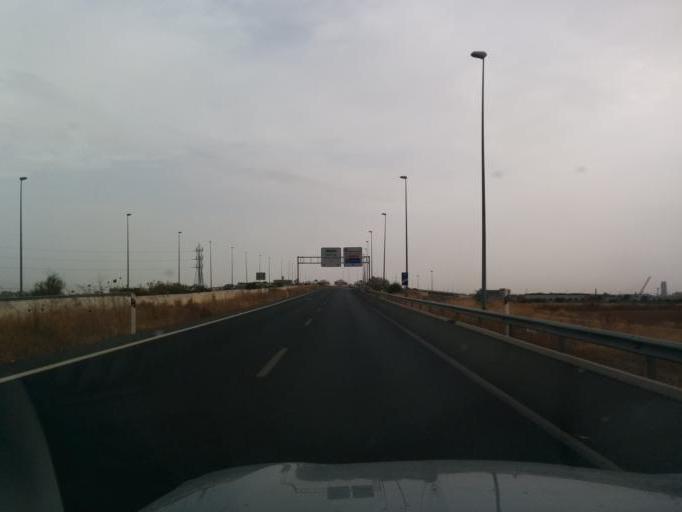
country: ES
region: Andalusia
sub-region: Provincia de Sevilla
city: La Algaba
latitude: 37.4420
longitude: -5.9717
